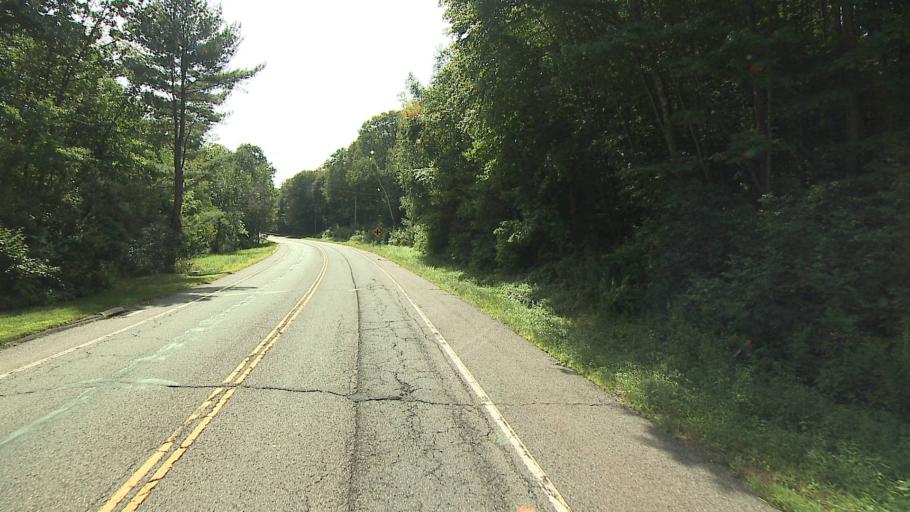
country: US
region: Connecticut
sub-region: Litchfield County
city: Thomaston
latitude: 41.6756
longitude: -73.0905
